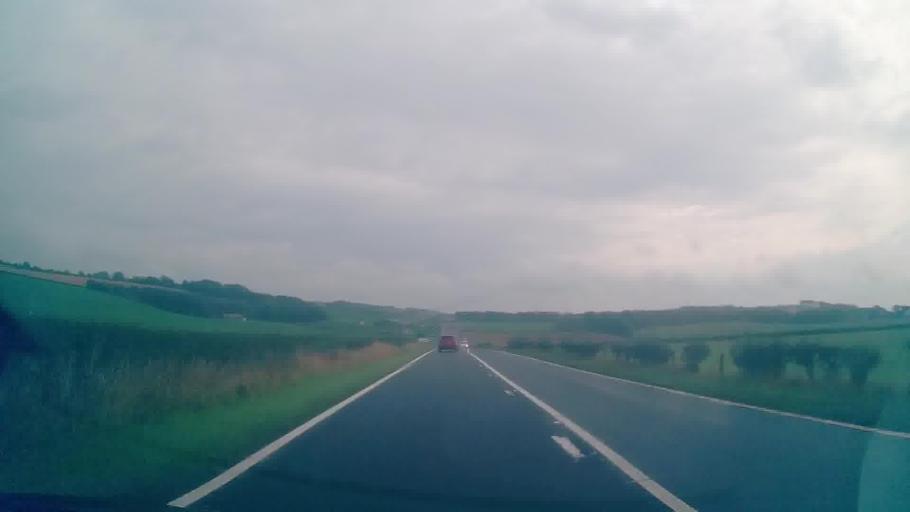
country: GB
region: Scotland
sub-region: Dumfries and Galloway
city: Lochmaben
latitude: 55.0461
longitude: -3.4534
